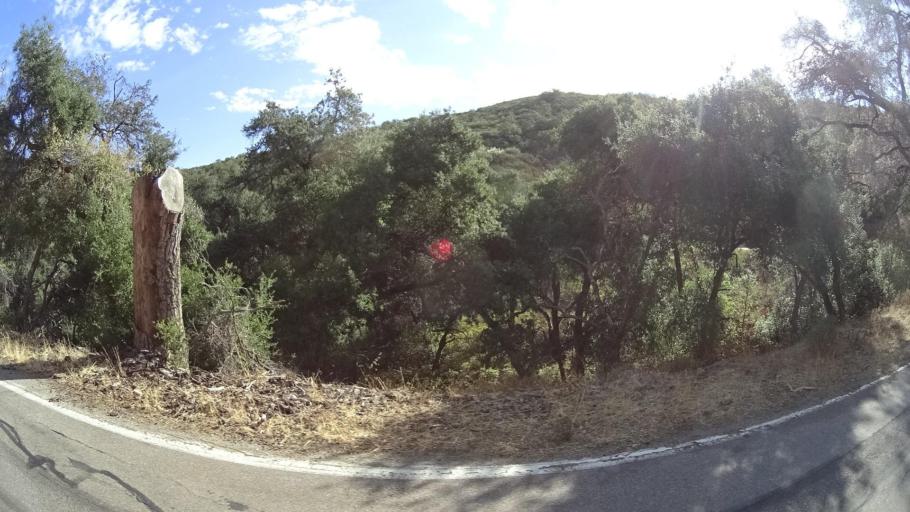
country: US
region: California
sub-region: San Diego County
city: Ramona
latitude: 33.1940
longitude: -116.7734
